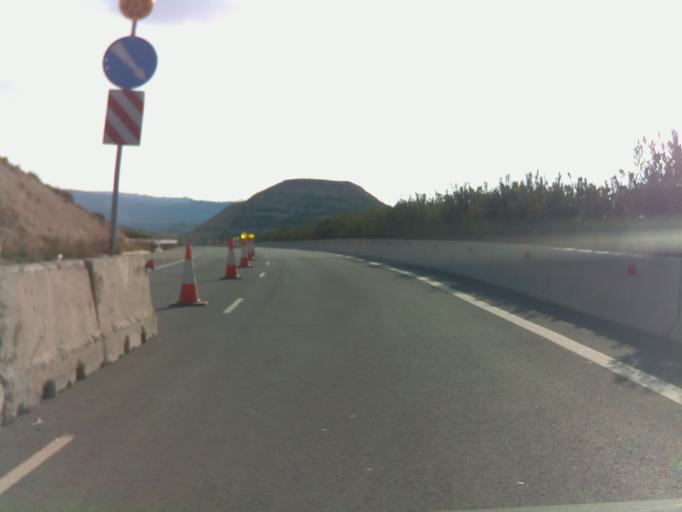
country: CY
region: Limassol
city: Pissouri
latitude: 34.6682
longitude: 32.6416
